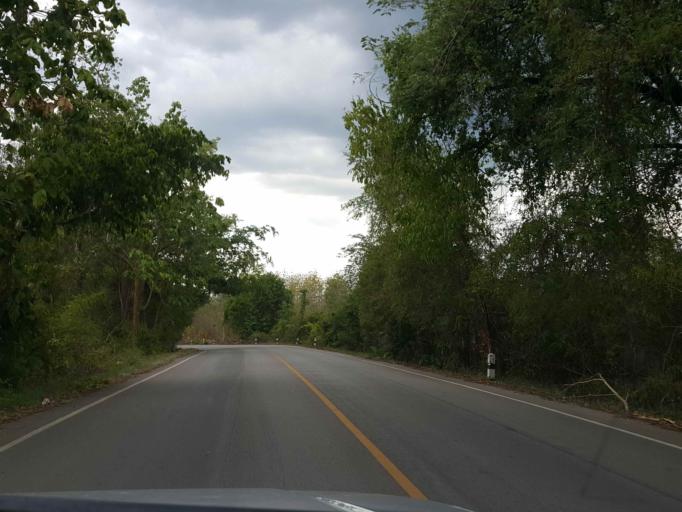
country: TH
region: Sukhothai
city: Thung Saliam
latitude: 17.3497
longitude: 99.4353
